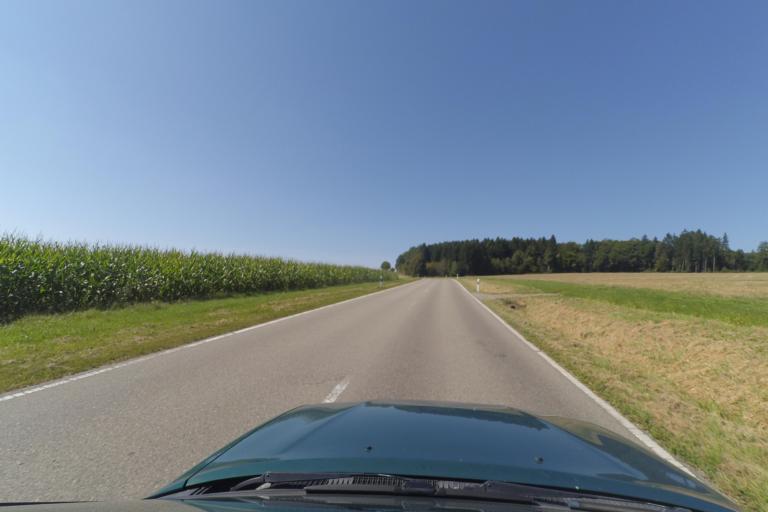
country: DE
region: Baden-Wuerttemberg
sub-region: Regierungsbezirk Stuttgart
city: Steinheim am Albuch
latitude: 48.7291
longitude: 10.0543
